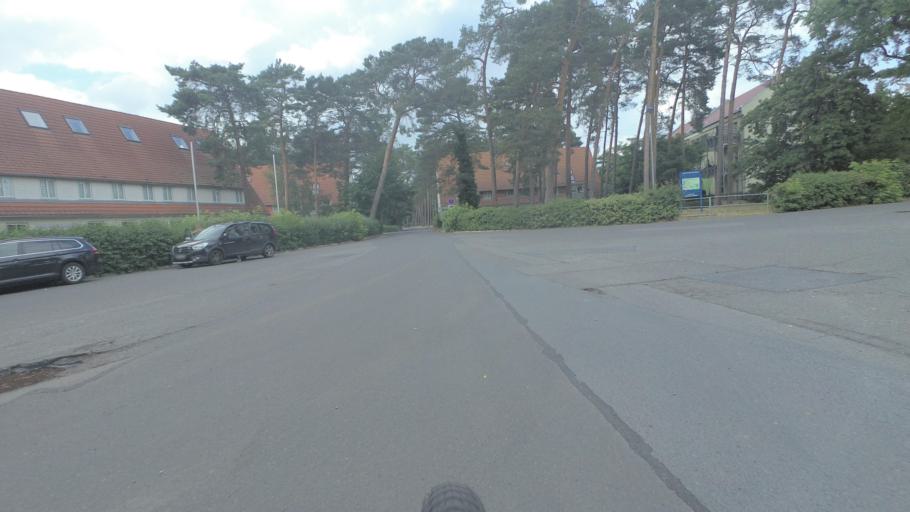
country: DE
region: Brandenburg
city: Zossen
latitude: 52.1905
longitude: 13.4695
